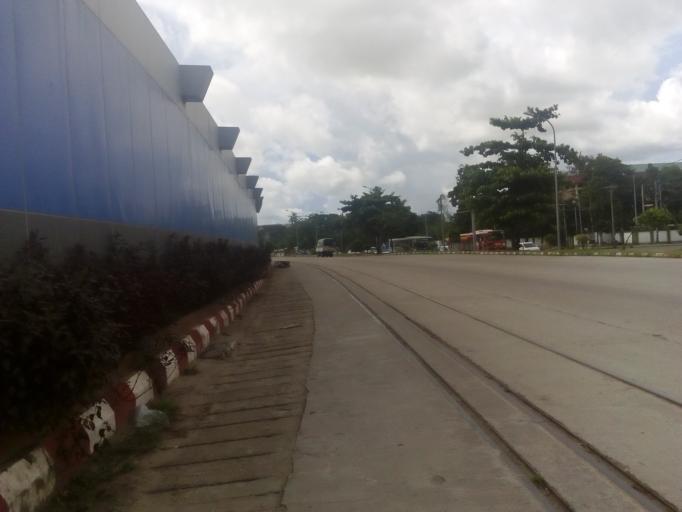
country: MM
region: Yangon
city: Yangon
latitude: 16.7788
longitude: 96.1347
